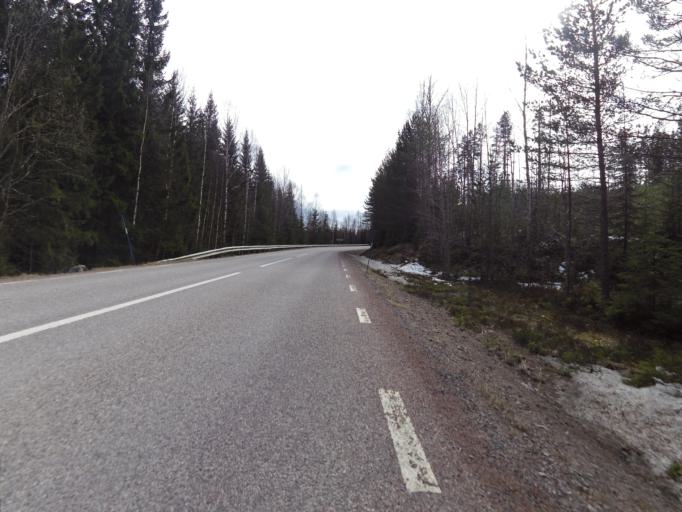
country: SE
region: Dalarna
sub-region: Hedemora Kommun
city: Langshyttan
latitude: 60.5405
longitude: 16.1289
